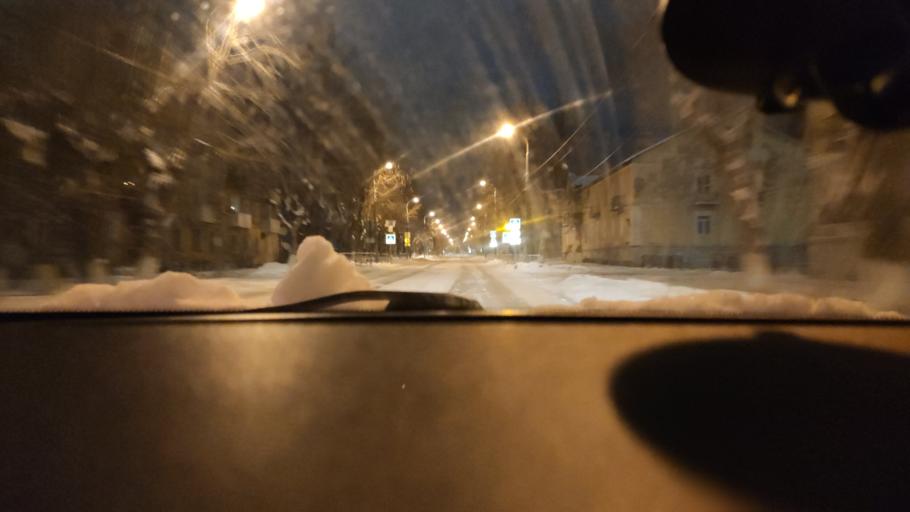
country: RU
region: Perm
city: Krasnokamsk
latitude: 58.0813
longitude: 55.7453
